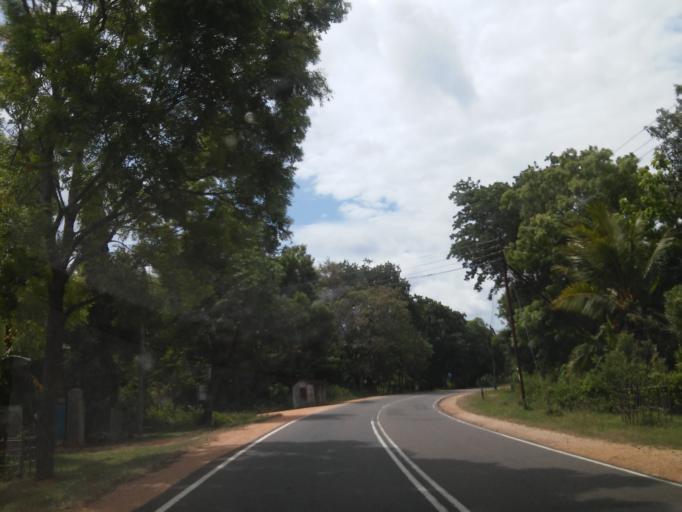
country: LK
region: Central
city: Sigiriya
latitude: 8.0703
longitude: 80.6945
